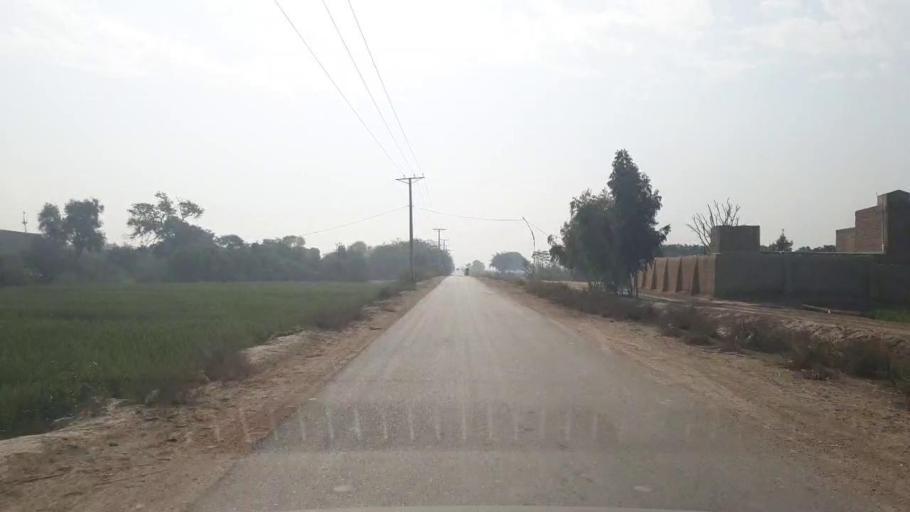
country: PK
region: Sindh
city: Hala
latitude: 25.7840
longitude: 68.4422
